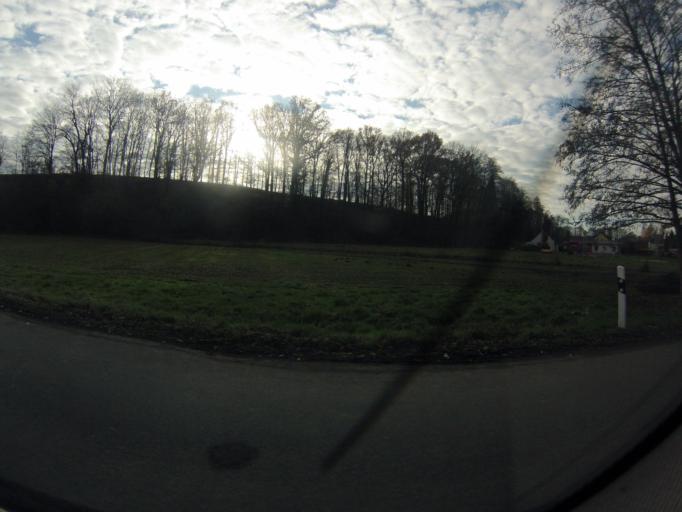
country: DE
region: Thuringia
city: Heyersdorf
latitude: 50.8590
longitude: 12.3859
